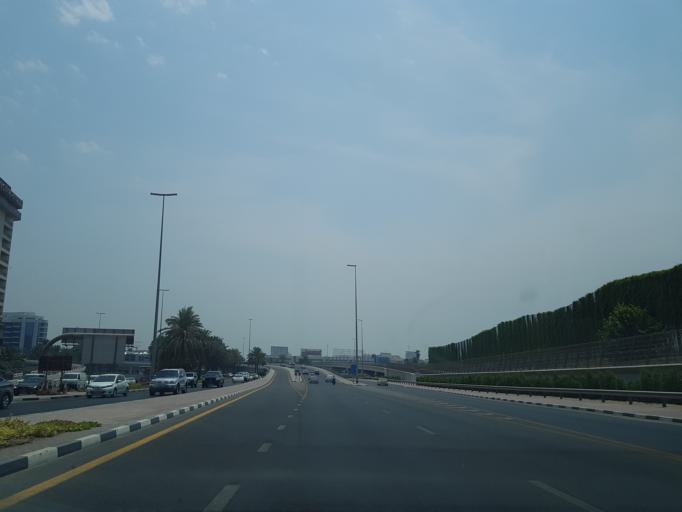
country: AE
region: Ash Shariqah
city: Sharjah
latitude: 25.2500
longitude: 55.3328
